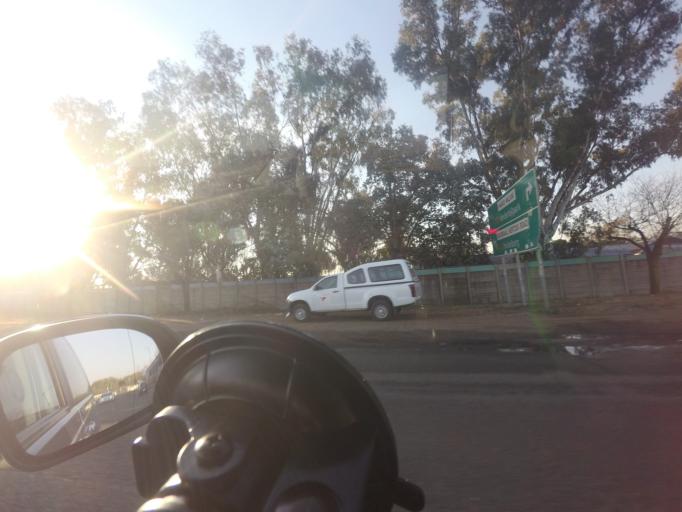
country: ZA
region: Gauteng
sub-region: Sedibeng District Municipality
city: Vereeniging
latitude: -26.6691
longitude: 27.9374
